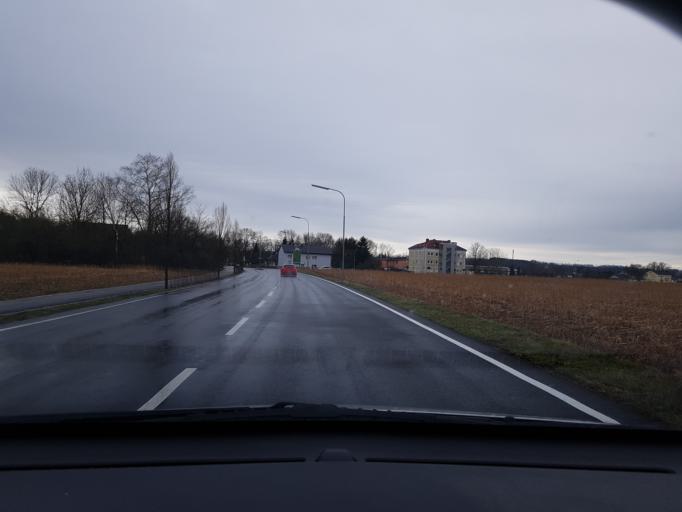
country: AT
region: Upper Austria
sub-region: Politischer Bezirk Linz-Land
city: Traun
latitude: 48.2173
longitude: 14.2188
